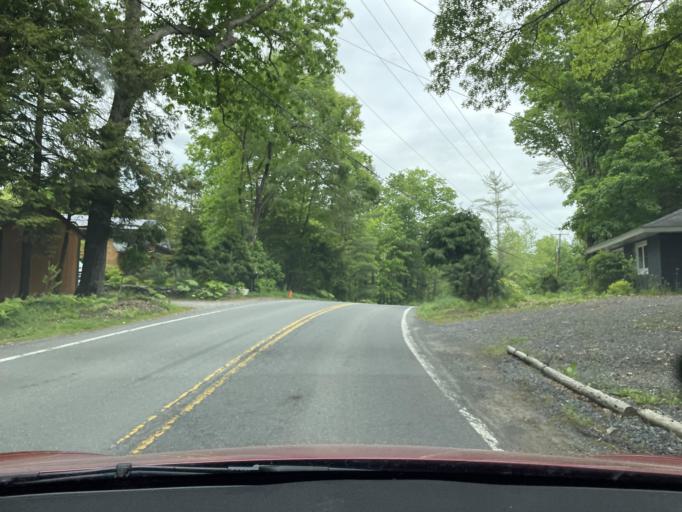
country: US
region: New York
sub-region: Ulster County
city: Zena
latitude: 42.0012
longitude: -74.0561
